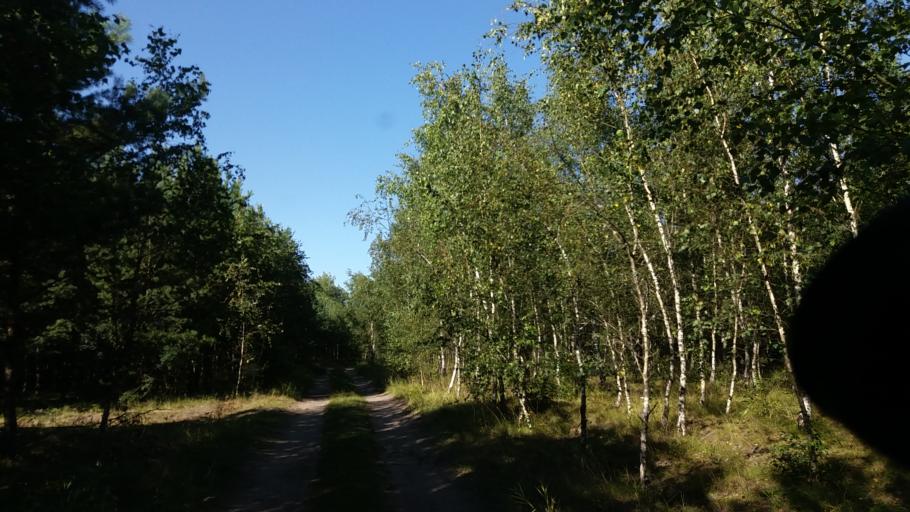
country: PL
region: West Pomeranian Voivodeship
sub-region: Powiat szczecinecki
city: Borne Sulinowo
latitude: 53.5797
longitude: 16.5233
